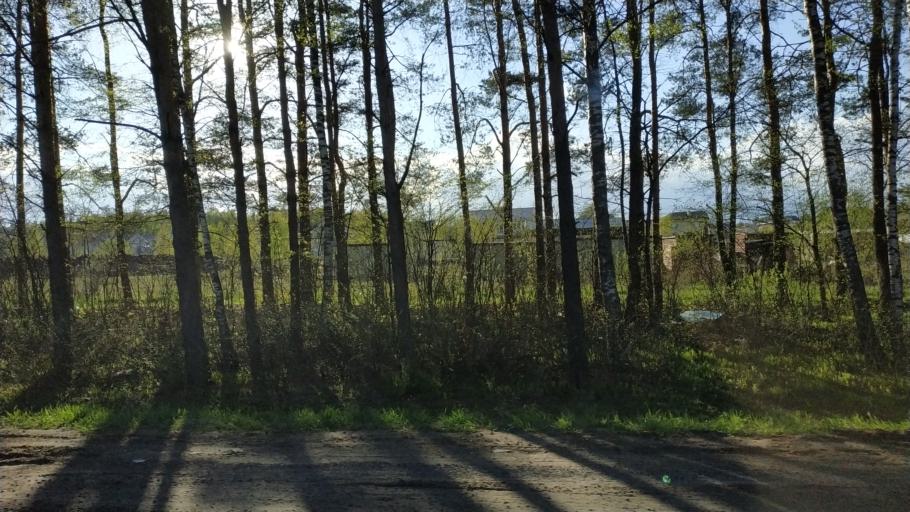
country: RU
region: Moskovskaya
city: Gzhel'
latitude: 55.6439
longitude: 38.3706
